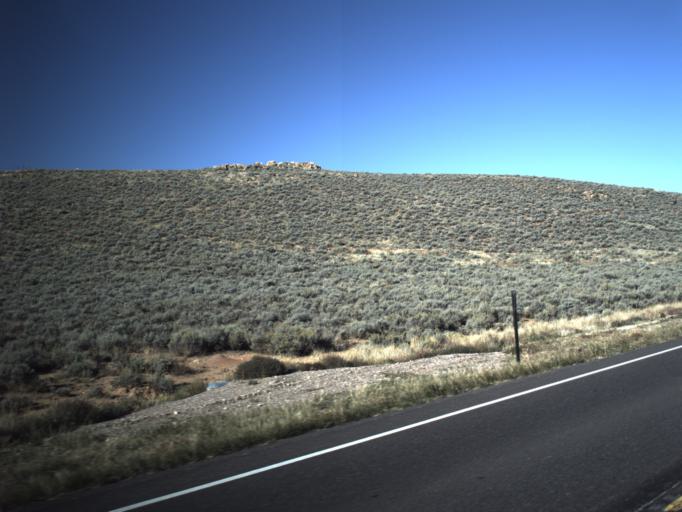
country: US
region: Utah
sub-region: Washington County
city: Enterprise
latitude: 37.7432
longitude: -113.7502
